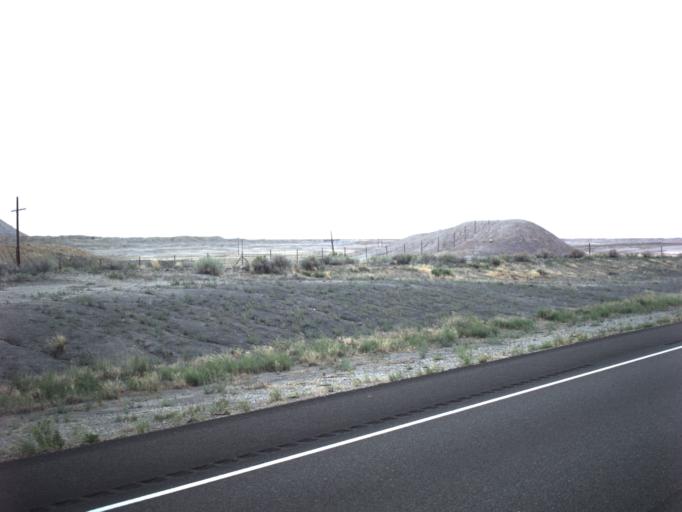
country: US
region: Utah
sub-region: Carbon County
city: East Carbon City
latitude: 39.0852
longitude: -110.3191
